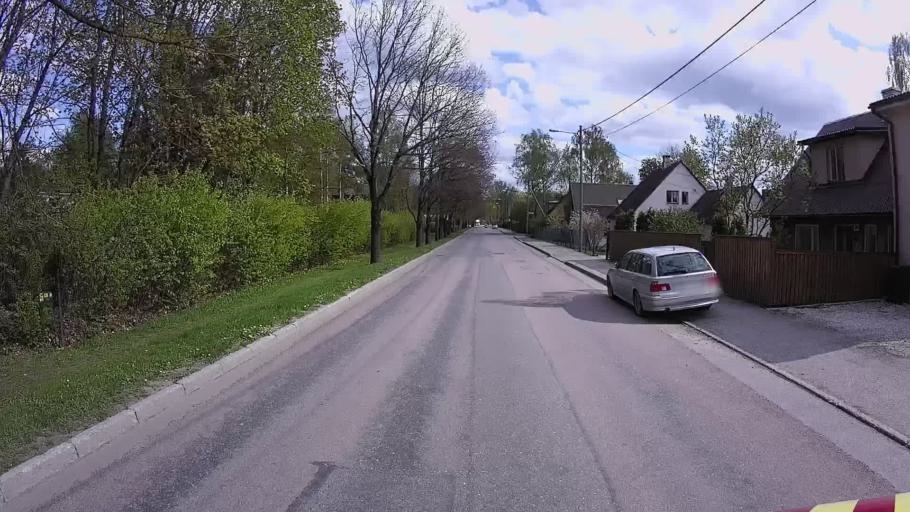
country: EE
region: Tartu
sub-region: Tartu linn
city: Tartu
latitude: 58.3990
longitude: 26.7312
